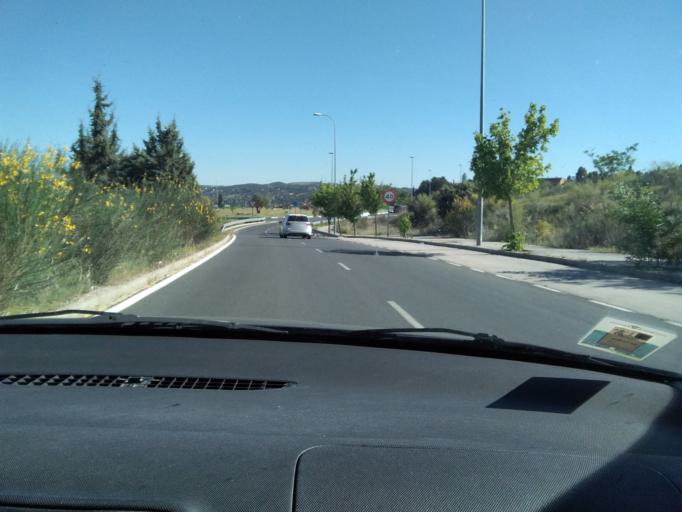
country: ES
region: Castille-La Mancha
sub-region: Province of Toledo
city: Toledo
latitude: 39.8891
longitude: -4.0555
